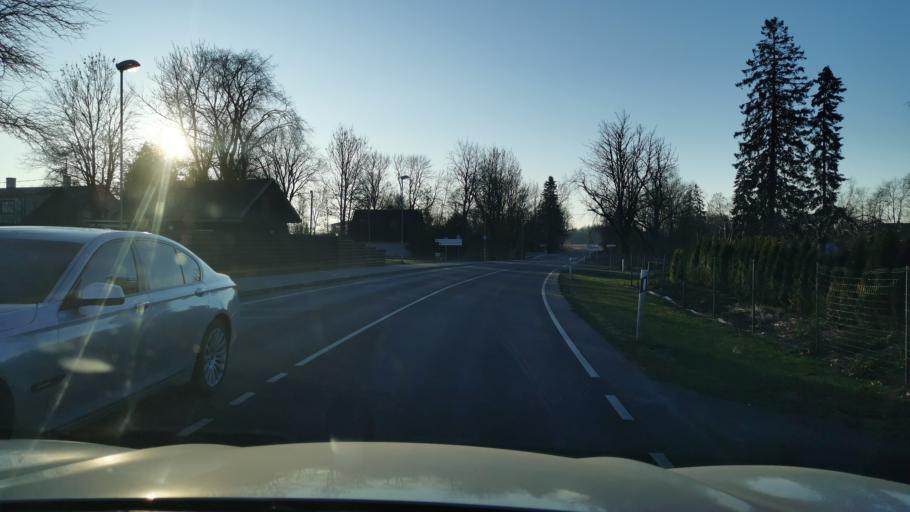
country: EE
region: Ida-Virumaa
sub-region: Kivioli linn
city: Kivioli
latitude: 59.3205
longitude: 27.0101
